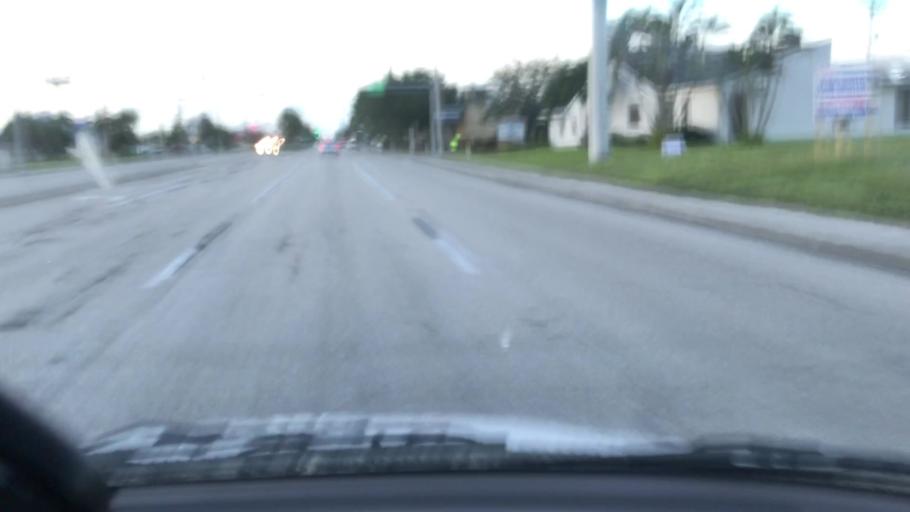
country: US
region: Florida
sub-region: Lee County
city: Cape Coral
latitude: 26.5925
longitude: -81.9418
